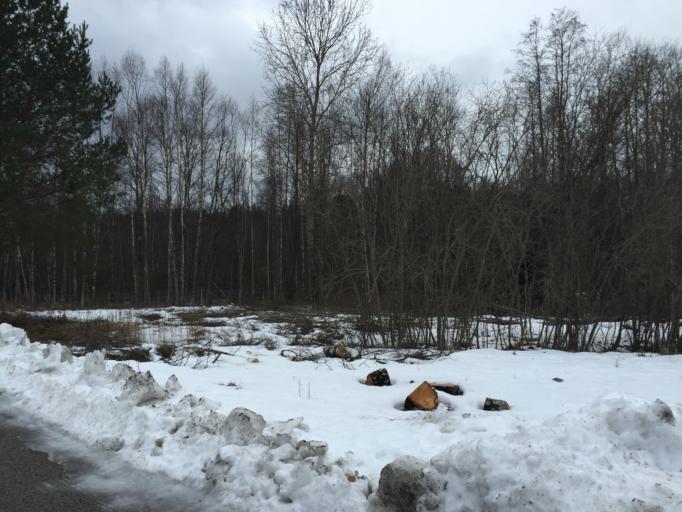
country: SE
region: Stockholm
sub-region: Salems Kommun
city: Ronninge
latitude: 59.2001
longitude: 17.7225
